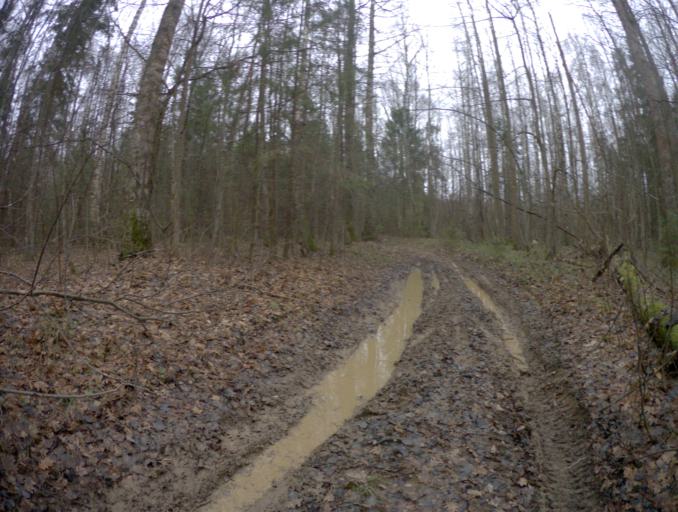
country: RU
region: Vladimir
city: Golovino
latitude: 56.0139
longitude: 40.5355
